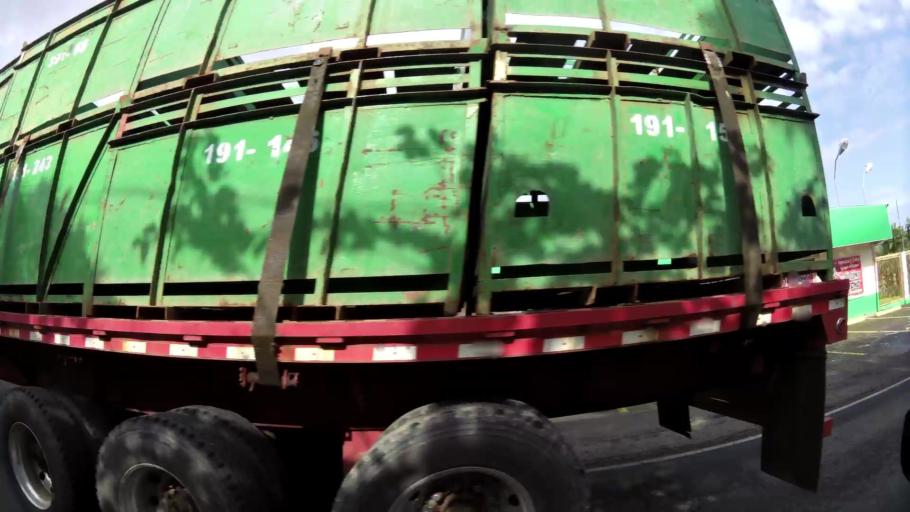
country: CR
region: Limon
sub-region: Canton de Guacimo
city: Guacimo
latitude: 10.2113
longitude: -83.6836
